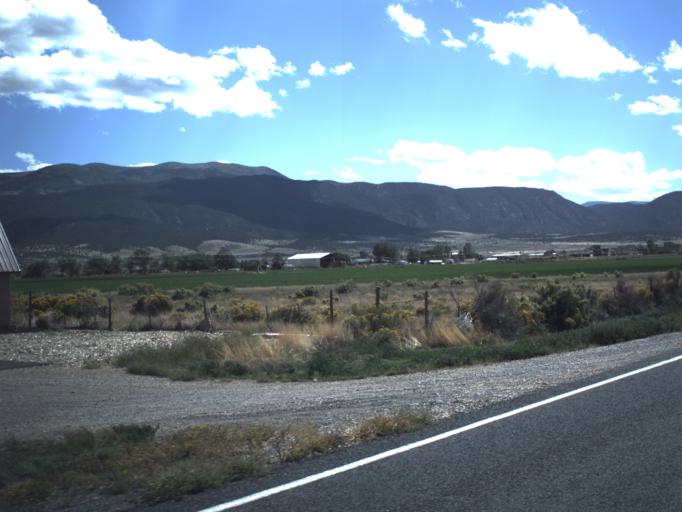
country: US
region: Utah
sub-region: Iron County
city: Enoch
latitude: 37.7758
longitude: -113.0553
